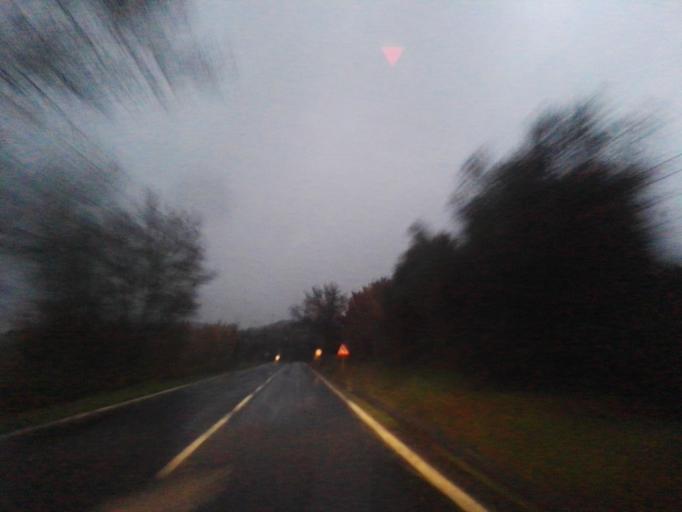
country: PT
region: Santarem
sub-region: Cartaxo
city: Cartaxo
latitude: 39.2684
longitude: -8.8011
